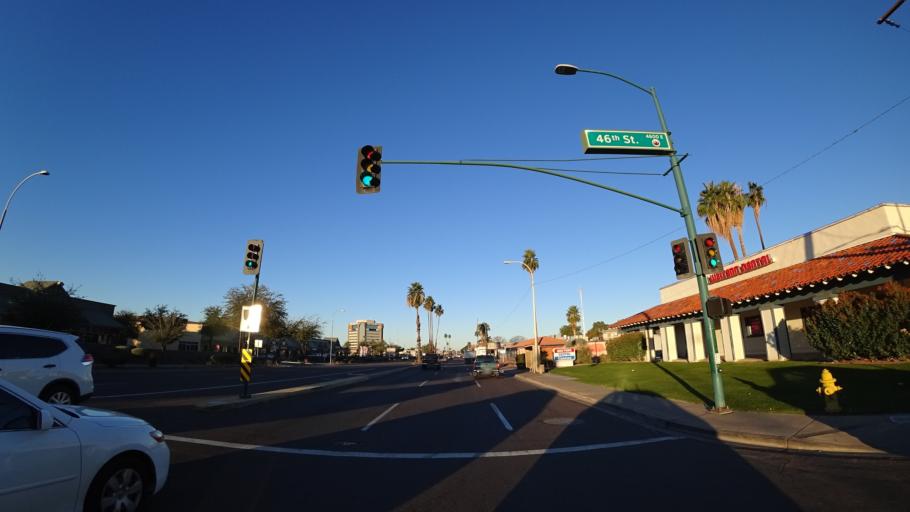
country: US
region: Arizona
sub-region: Maricopa County
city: Paradise Valley
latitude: 33.4803
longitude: -111.9826
